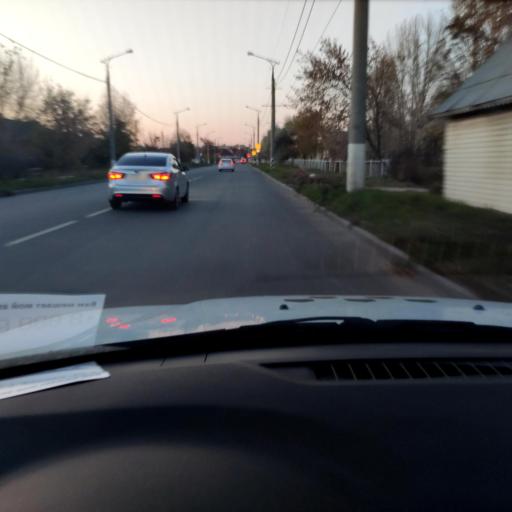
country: RU
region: Samara
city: Tol'yatti
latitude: 53.5131
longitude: 49.3953
